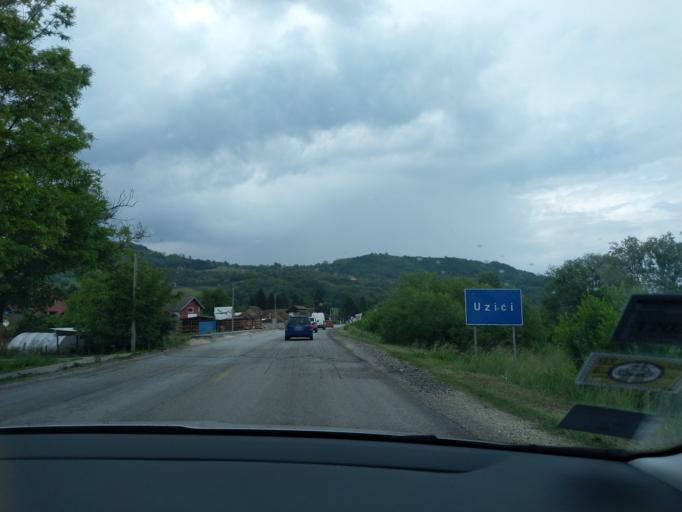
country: RS
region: Central Serbia
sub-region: Zlatiborski Okrug
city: Pozega
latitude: 43.8110
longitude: 19.9757
